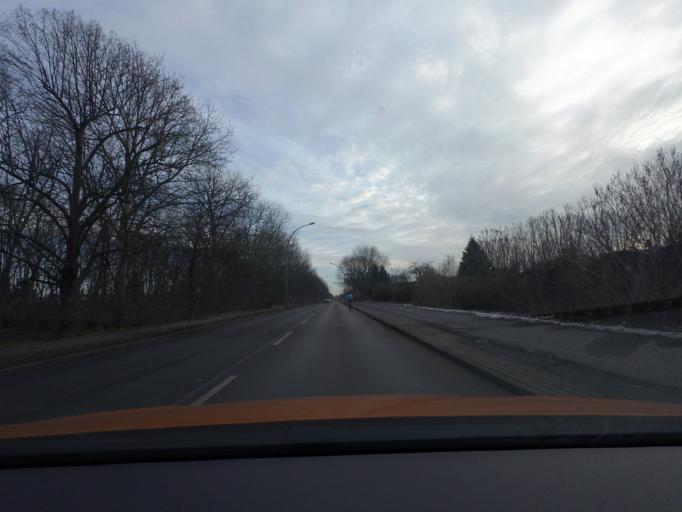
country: DE
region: Berlin
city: Blankenfelde
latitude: 52.6293
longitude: 13.3830
